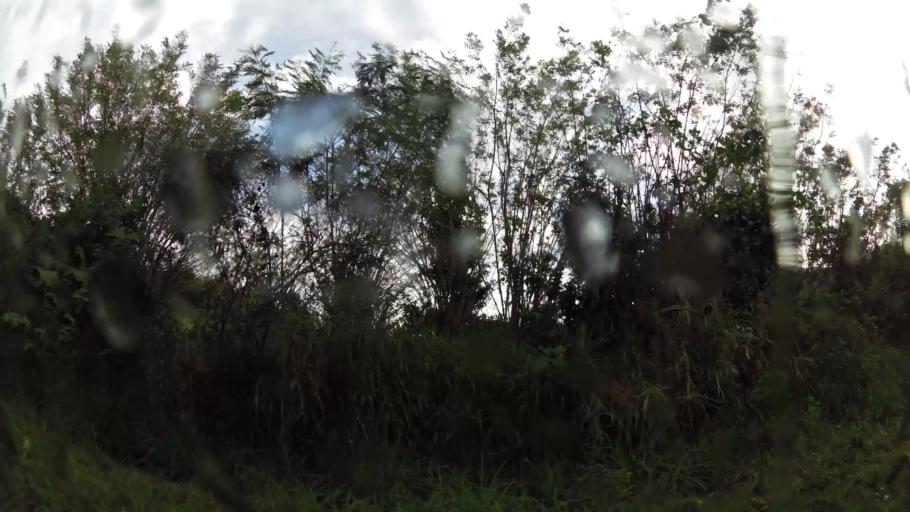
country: MQ
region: Martinique
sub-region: Martinique
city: Les Trois-Ilets
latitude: 14.5414
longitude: -61.0479
